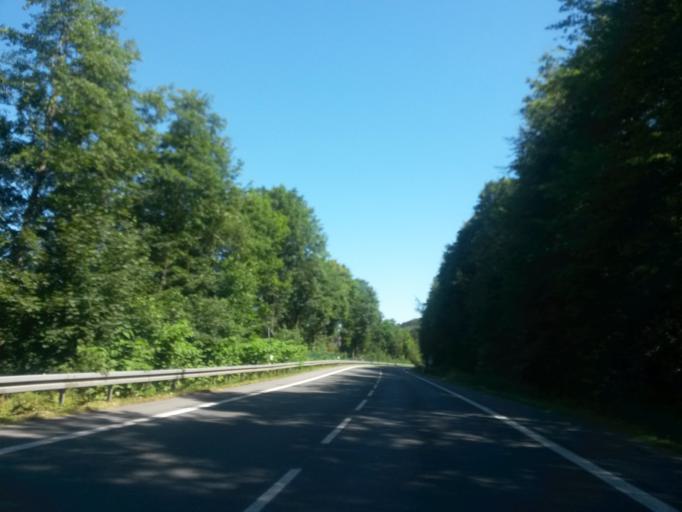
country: DE
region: North Rhine-Westphalia
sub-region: Regierungsbezirk Arnsberg
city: Luedenscheid
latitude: 51.2199
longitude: 7.6576
